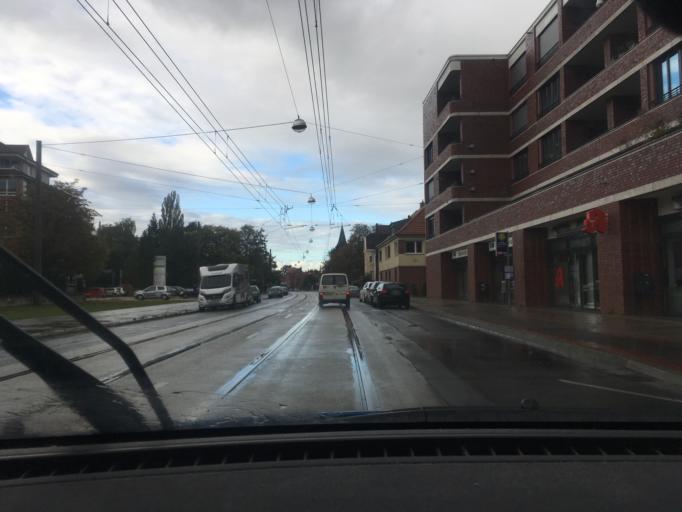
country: DE
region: Lower Saxony
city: Langenhagen
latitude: 52.4108
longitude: 9.7992
